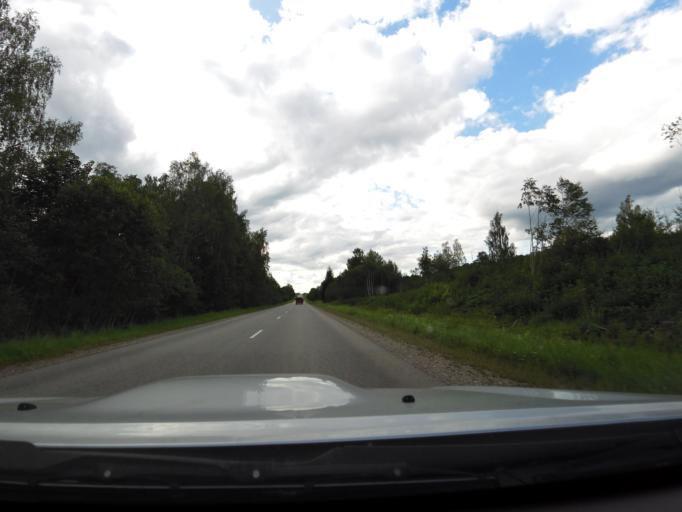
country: LV
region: Ilukste
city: Ilukste
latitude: 55.9679
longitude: 26.0366
